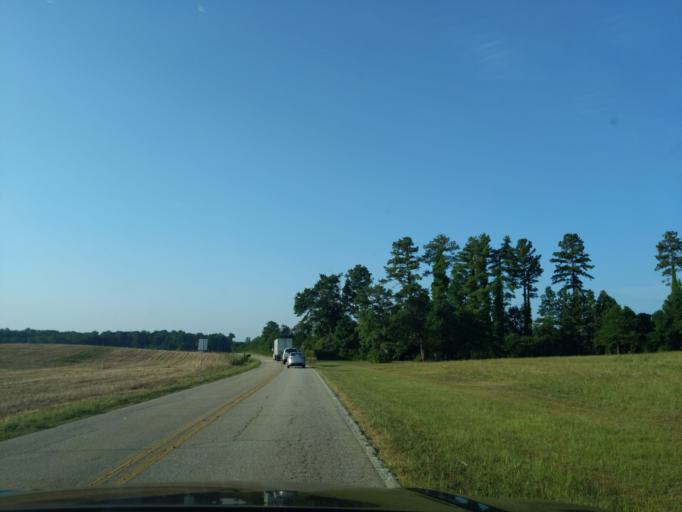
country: US
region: South Carolina
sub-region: Spartanburg County
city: Roebuck
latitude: 34.8169
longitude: -81.9862
